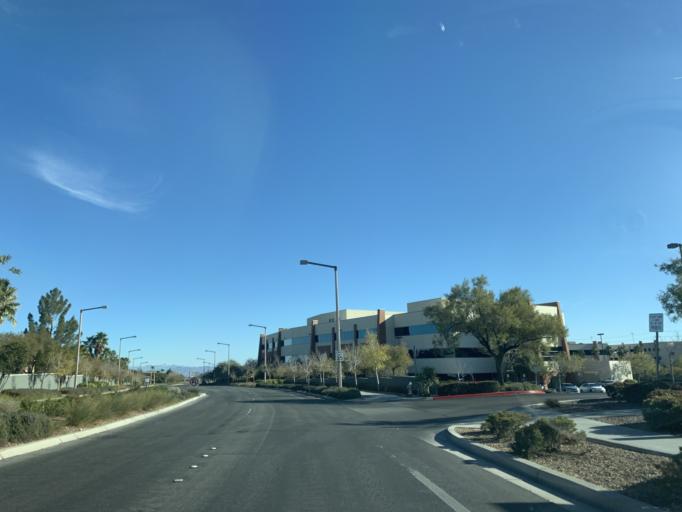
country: US
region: Nevada
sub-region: Clark County
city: Summerlin South
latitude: 36.1232
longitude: -115.3246
